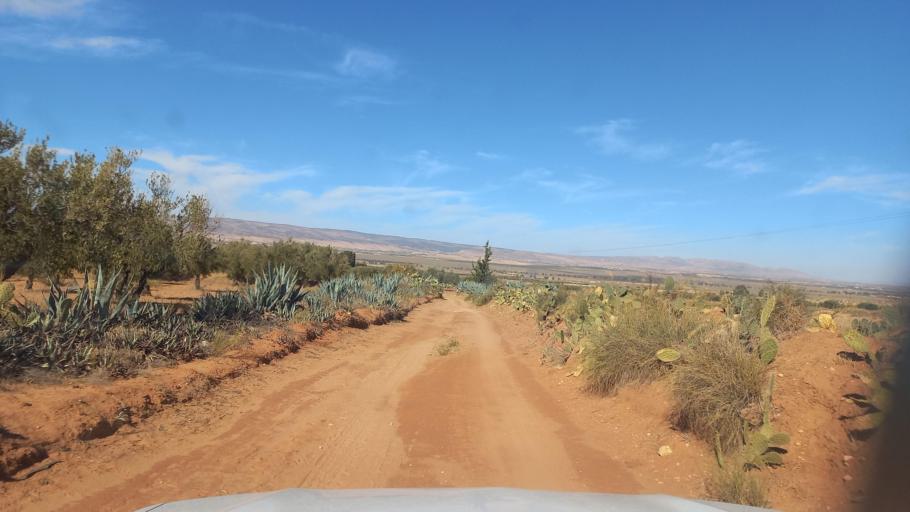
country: TN
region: Al Qasrayn
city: Kasserine
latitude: 35.2027
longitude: 8.9705
